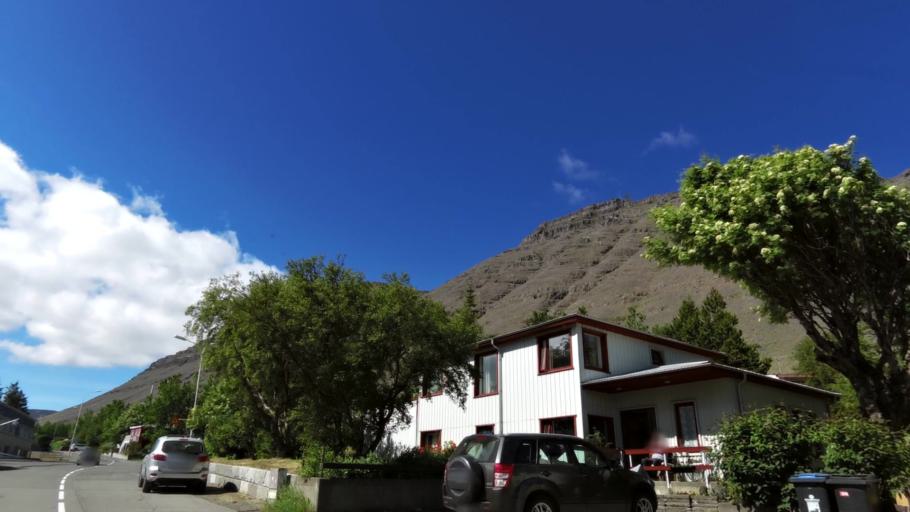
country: IS
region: Westfjords
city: Isafjoerdur
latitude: 65.6858
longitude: -23.6003
